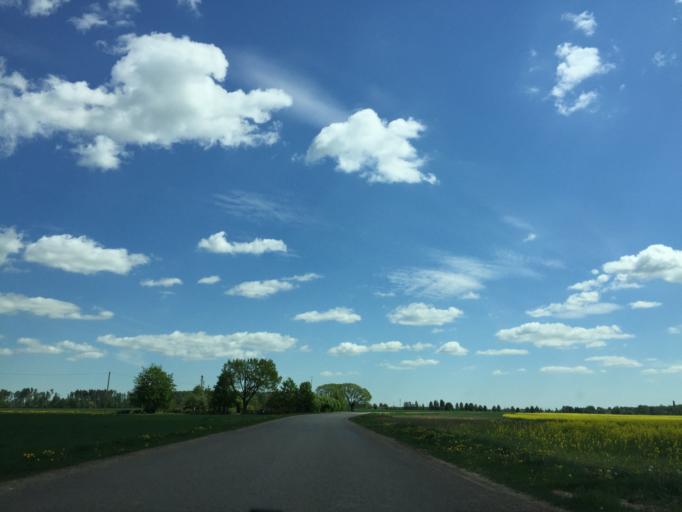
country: LV
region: Rundales
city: Pilsrundale
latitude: 56.4289
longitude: 24.0921
